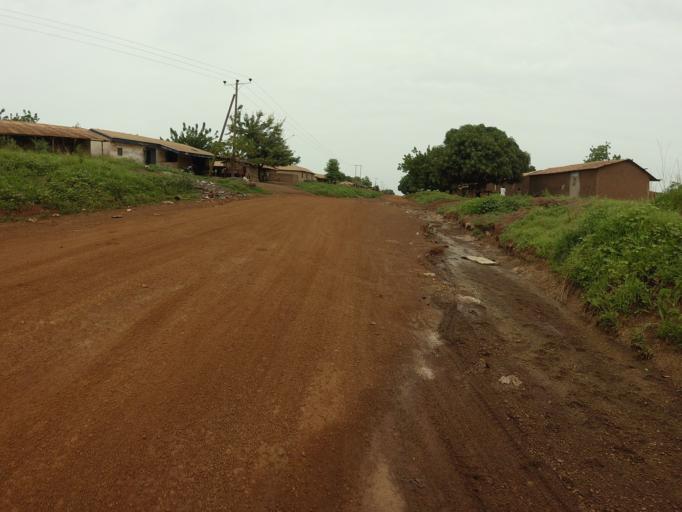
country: GH
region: Northern
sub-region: Yendi
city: Yendi
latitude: 9.0595
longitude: -0.0119
